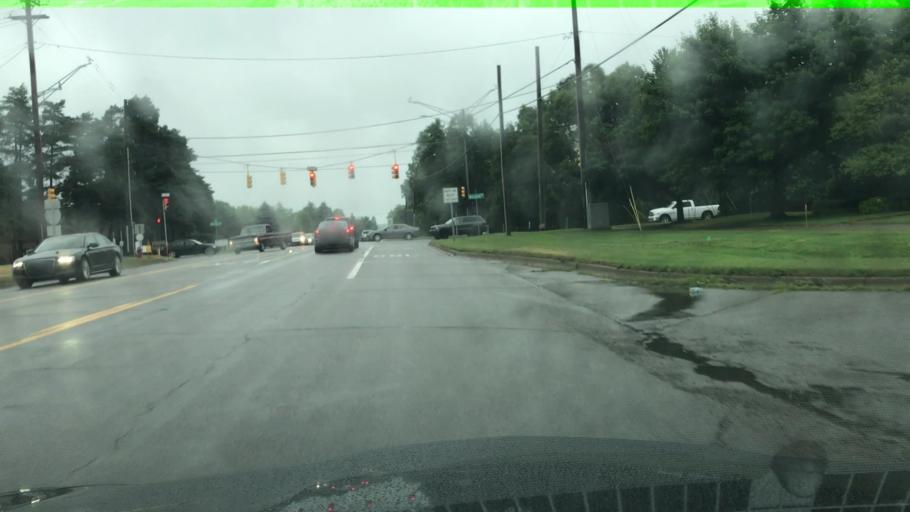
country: US
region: Michigan
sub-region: Oakland County
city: Lake Orion
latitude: 42.7355
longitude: -83.3079
